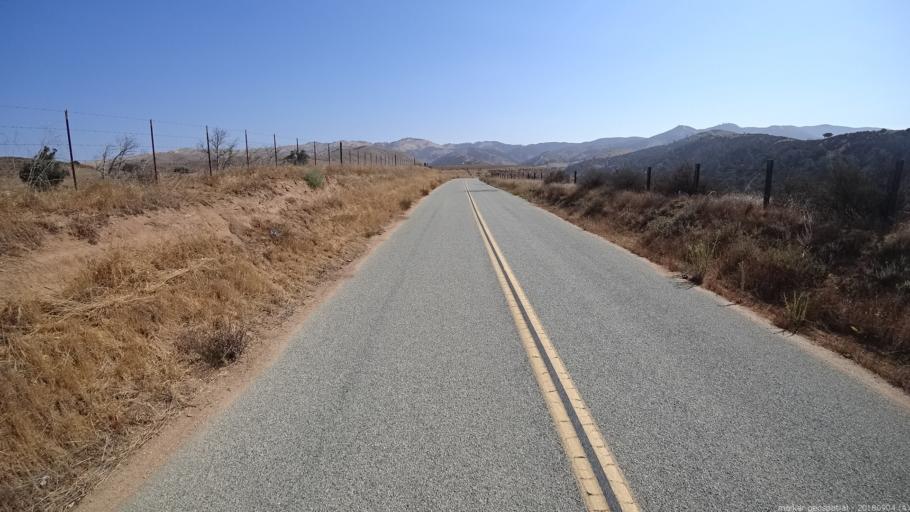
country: US
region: California
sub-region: Monterey County
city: Soledad
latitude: 36.5123
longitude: -121.3517
